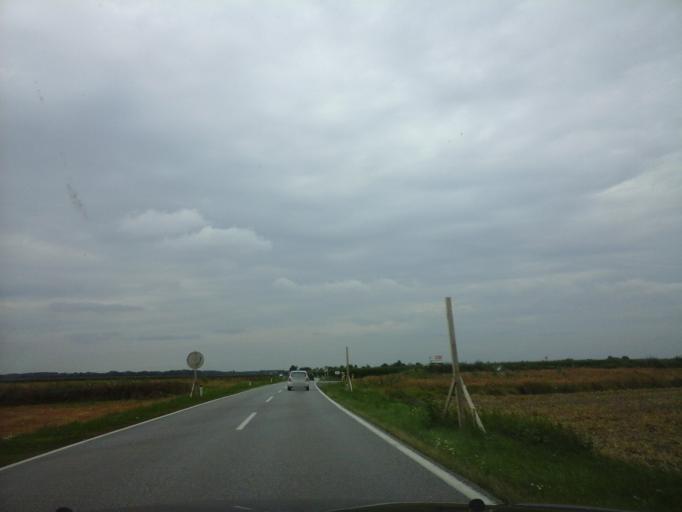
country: AT
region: Lower Austria
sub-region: Politischer Bezirk Ganserndorf
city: Orth an der Donau
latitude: 48.1568
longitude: 16.7390
